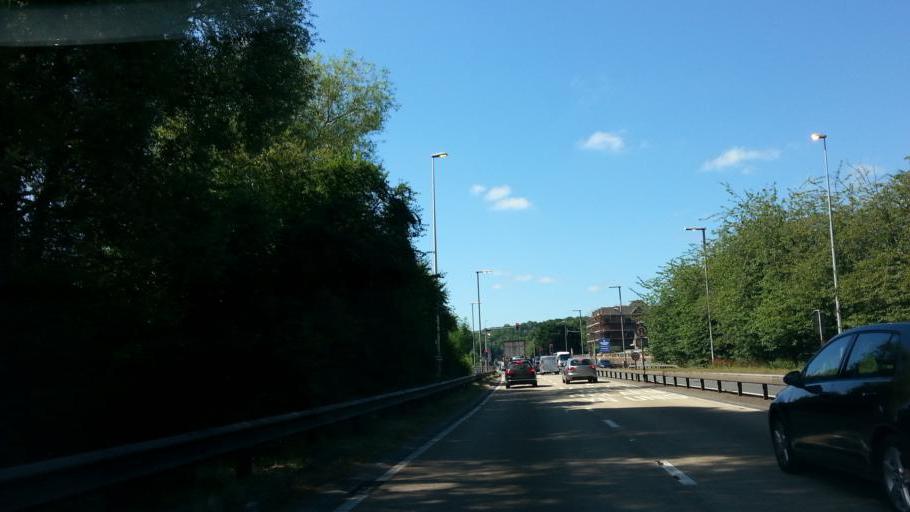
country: GB
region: Wales
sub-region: Monmouthshire
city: Monmouth
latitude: 51.8127
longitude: -2.7095
